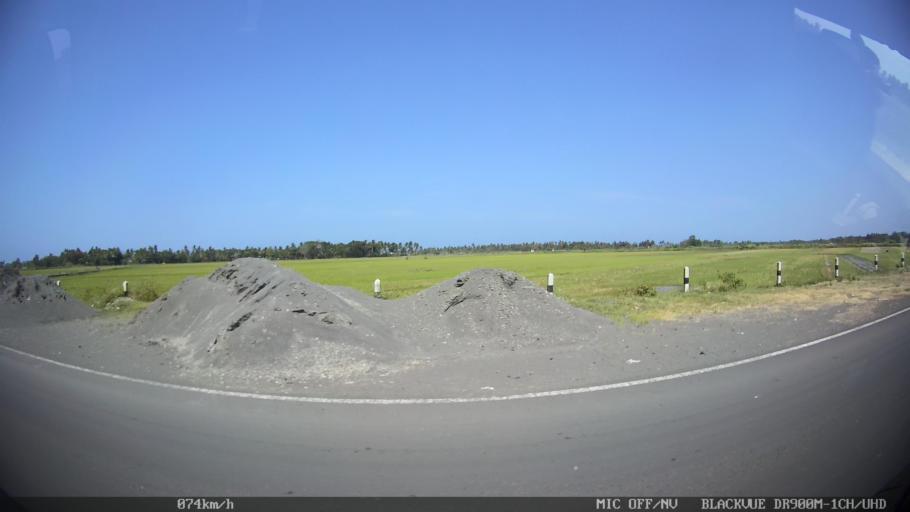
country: ID
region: Daerah Istimewa Yogyakarta
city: Srandakan
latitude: -7.9661
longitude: 110.2062
